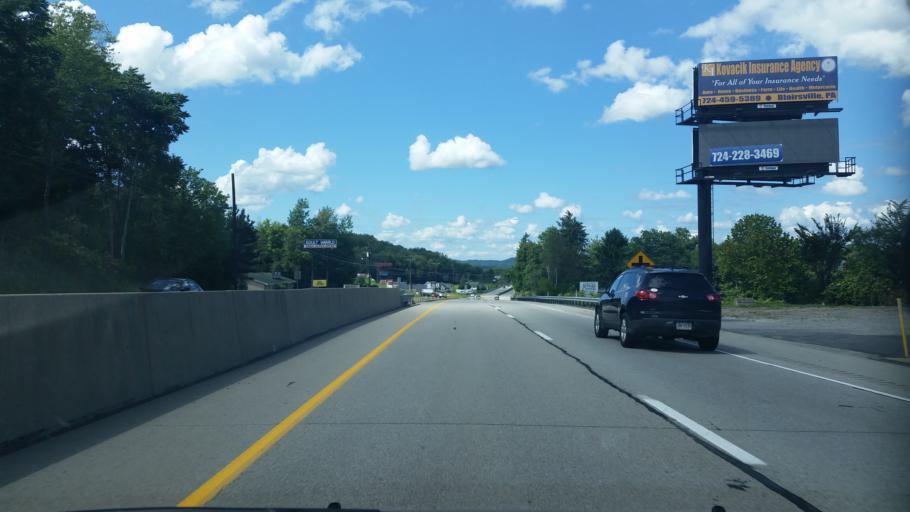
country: US
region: Pennsylvania
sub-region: Indiana County
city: Blairsville
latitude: 40.4415
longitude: -79.2421
